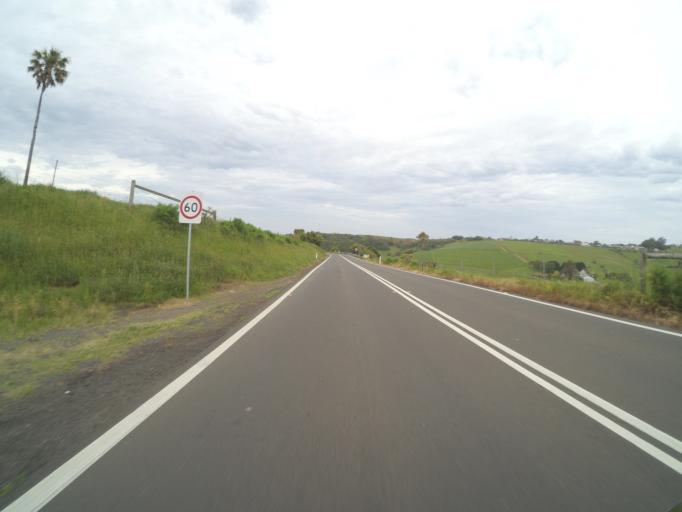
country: AU
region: New South Wales
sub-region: Kiama
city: Kiama
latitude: -34.6671
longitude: 150.8326
